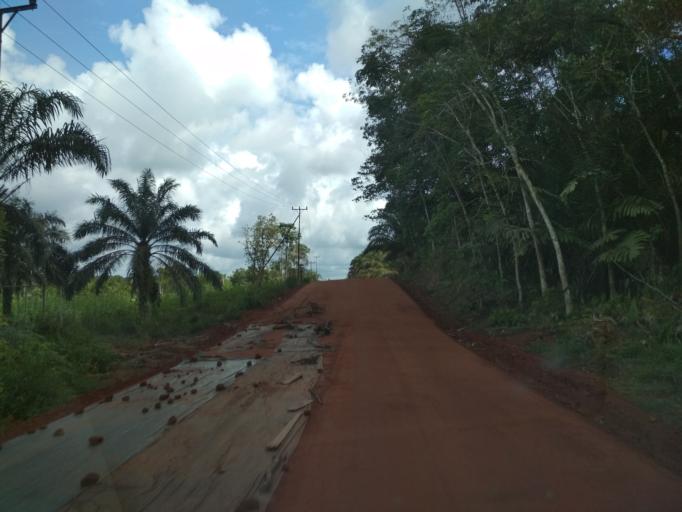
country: ID
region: West Kalimantan
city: Tayan
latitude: 0.5420
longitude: 110.0897
